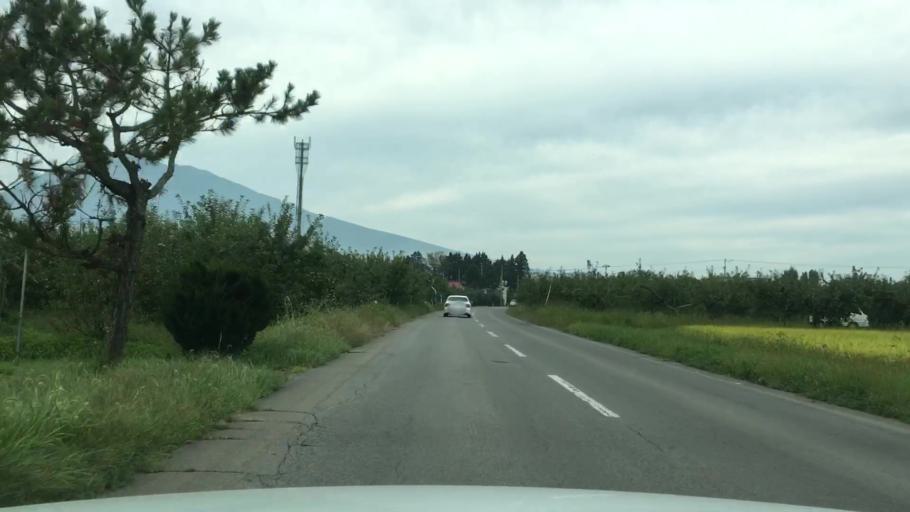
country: JP
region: Aomori
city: Hirosaki
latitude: 40.6438
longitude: 140.4277
